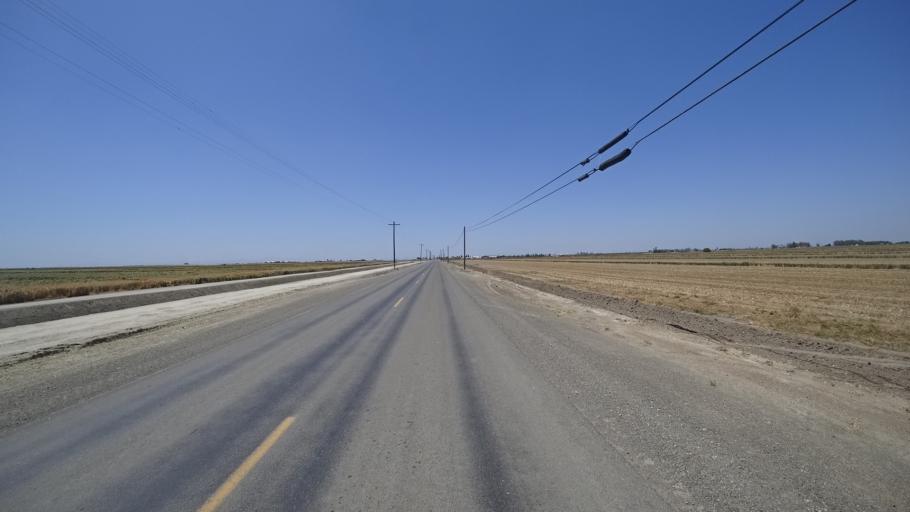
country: US
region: California
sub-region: Kings County
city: Home Garden
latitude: 36.1966
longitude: -119.6237
